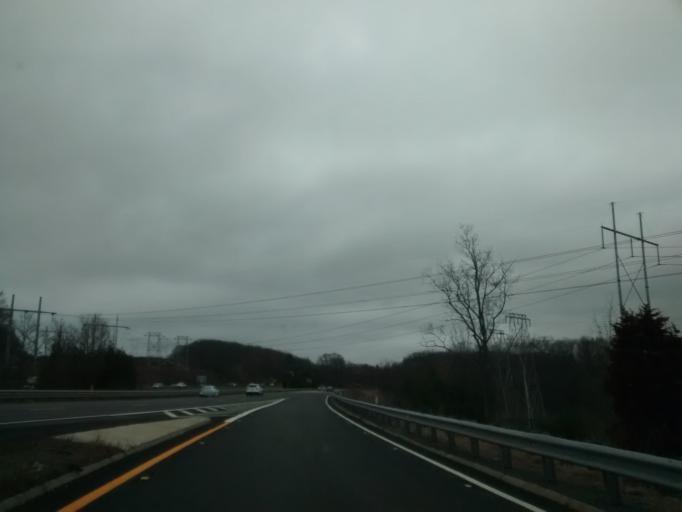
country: US
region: Massachusetts
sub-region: Worcester County
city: Milford
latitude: 42.1680
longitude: -71.5110
